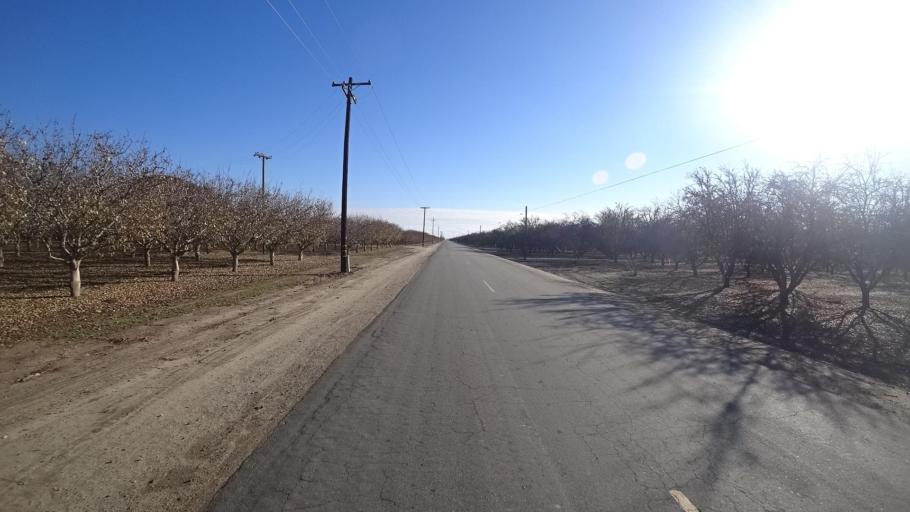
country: US
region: California
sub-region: Kern County
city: McFarland
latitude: 35.6887
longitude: -119.2996
